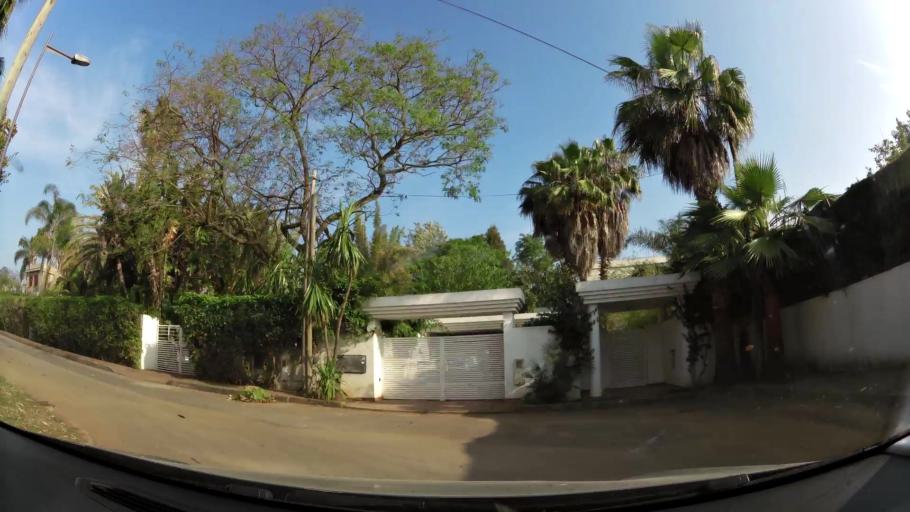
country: MA
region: Rabat-Sale-Zemmour-Zaer
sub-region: Rabat
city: Rabat
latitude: 33.9402
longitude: -6.8193
